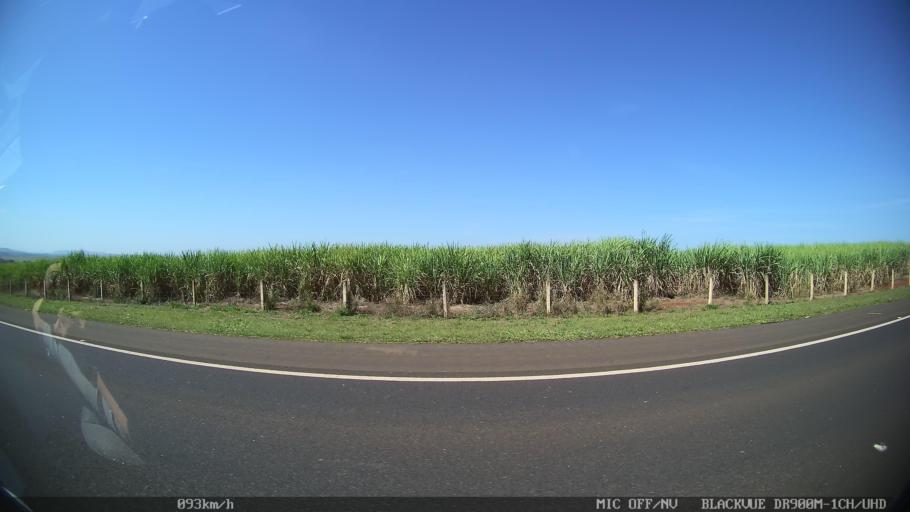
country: BR
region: Sao Paulo
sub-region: Batatais
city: Batatais
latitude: -20.7735
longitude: -47.5431
